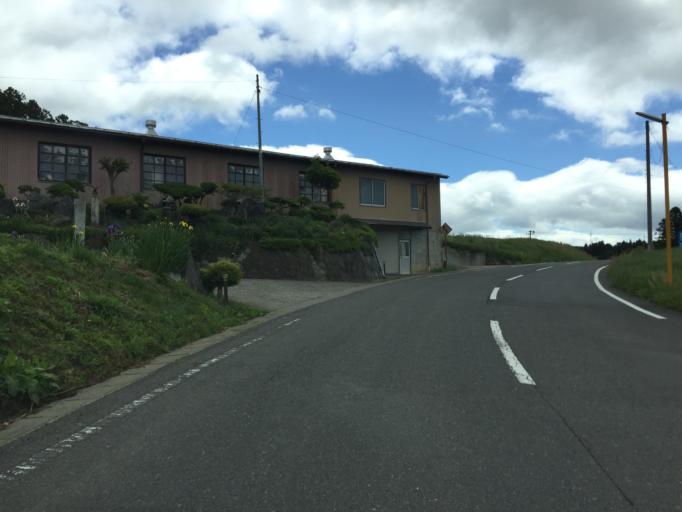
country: JP
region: Fukushima
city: Miharu
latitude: 37.4848
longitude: 140.4645
